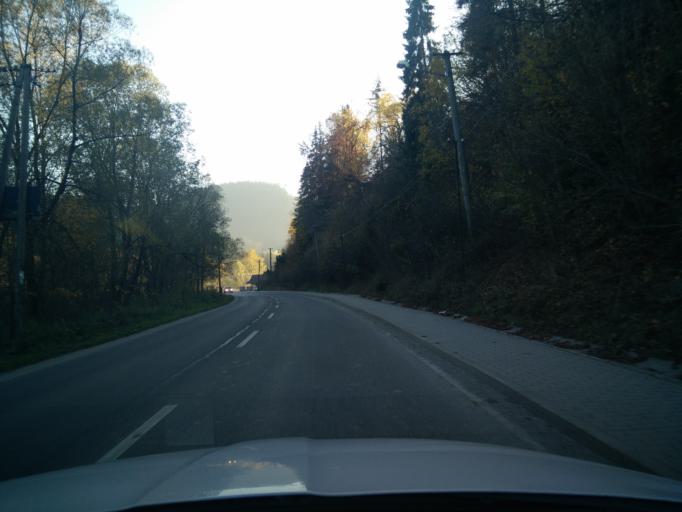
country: SK
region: Zilinsky
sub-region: Okres Zilina
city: Terchova
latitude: 49.3511
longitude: 19.0253
